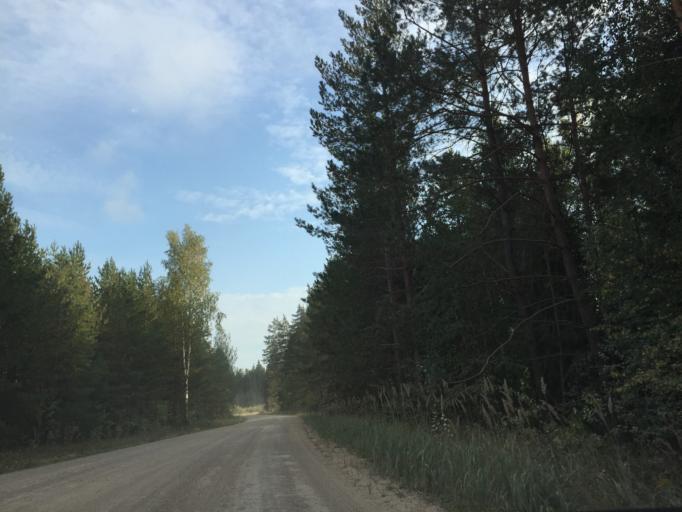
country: LV
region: Baldone
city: Baldone
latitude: 56.7929
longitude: 24.4395
